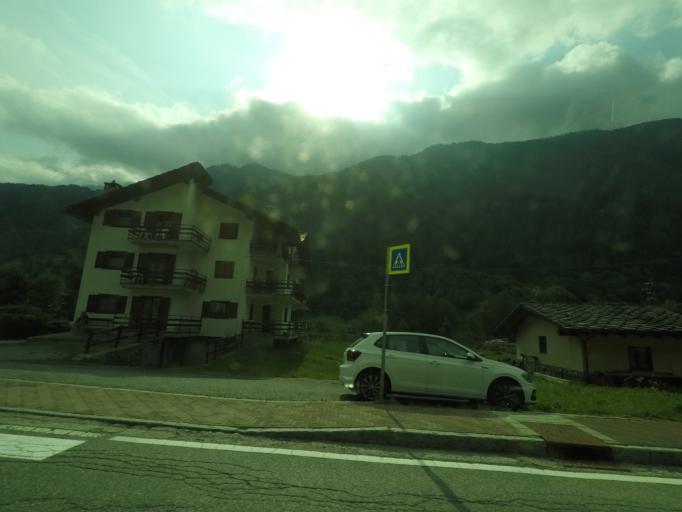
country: IT
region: Aosta Valley
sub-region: Valle d'Aosta
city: Valtournenche
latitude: 45.8648
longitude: 7.6115
